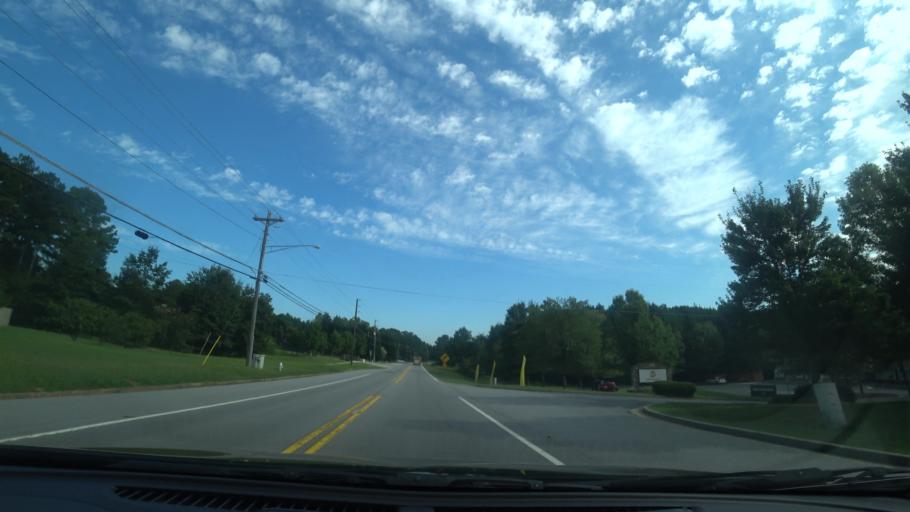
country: US
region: Georgia
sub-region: Gwinnett County
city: Grayson
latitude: 33.8348
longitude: -83.9605
